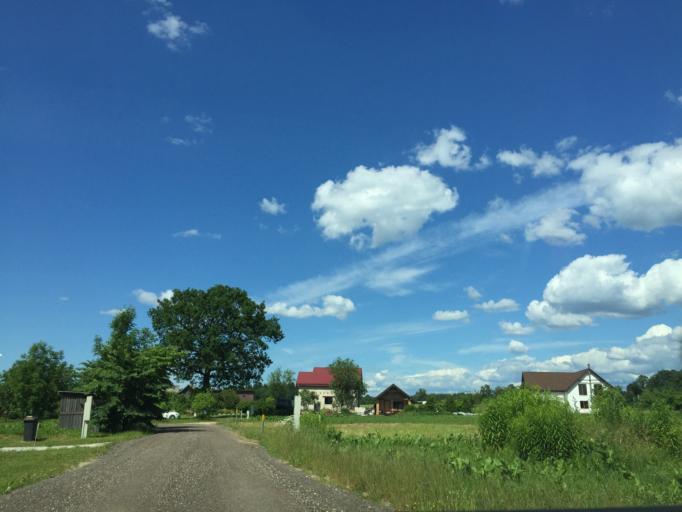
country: LV
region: Sigulda
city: Sigulda
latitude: 57.1669
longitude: 24.8855
